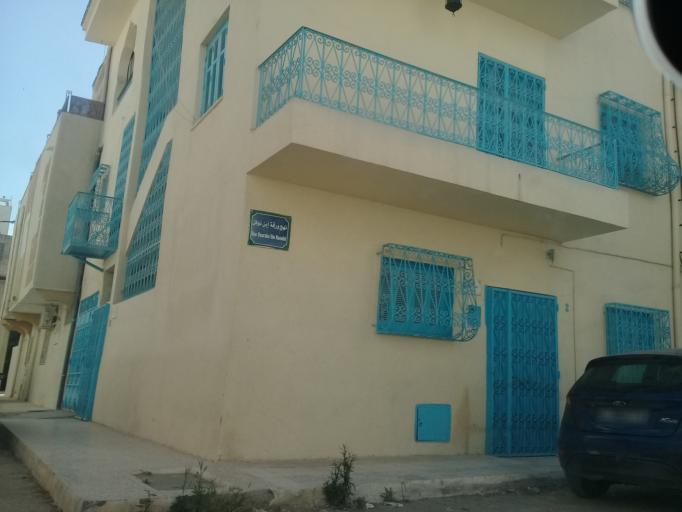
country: TN
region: Tunis
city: Tunis
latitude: 36.8315
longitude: 10.1907
